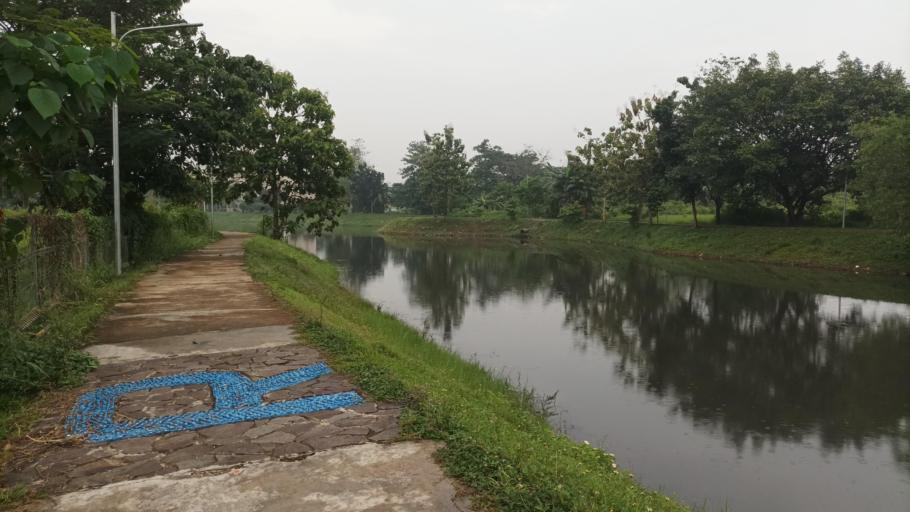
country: ID
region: West Java
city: Cileungsir
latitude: -6.3903
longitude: 106.9153
